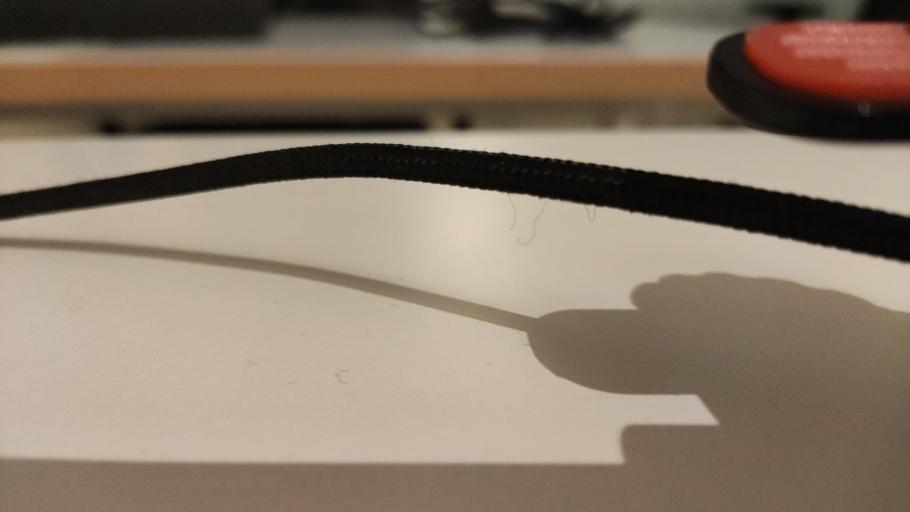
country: RU
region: Moskovskaya
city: Kurovskoye
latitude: 55.5438
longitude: 38.8732
